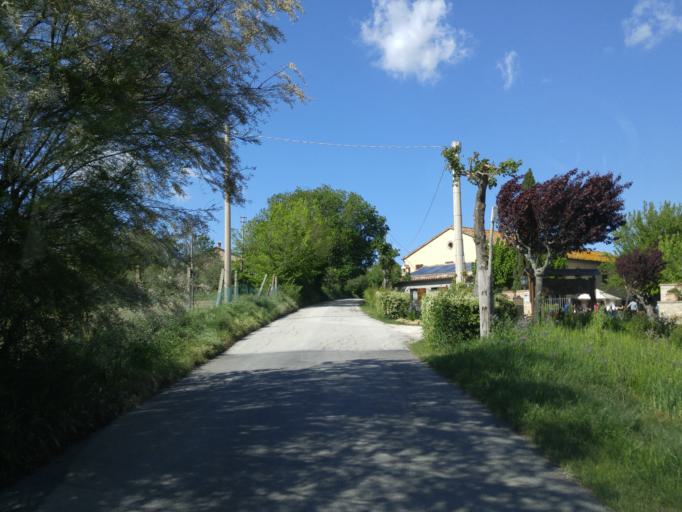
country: IT
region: The Marches
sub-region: Provincia di Pesaro e Urbino
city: Lucrezia
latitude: 43.7894
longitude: 12.9108
